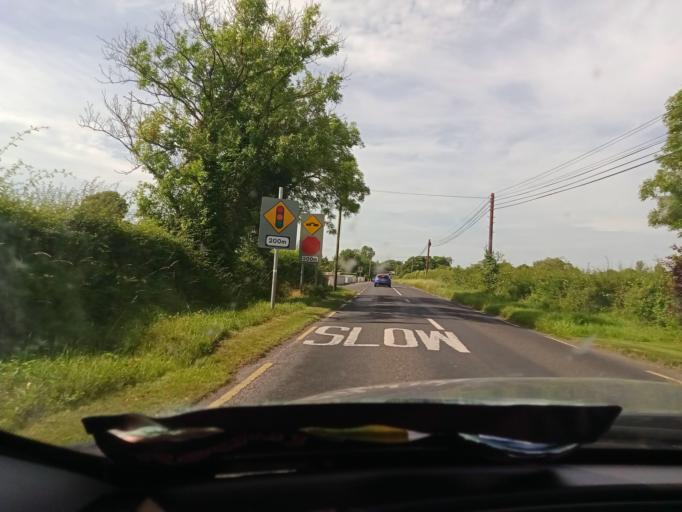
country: IE
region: Leinster
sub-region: Laois
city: Mountmellick
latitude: 53.1059
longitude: -7.3410
